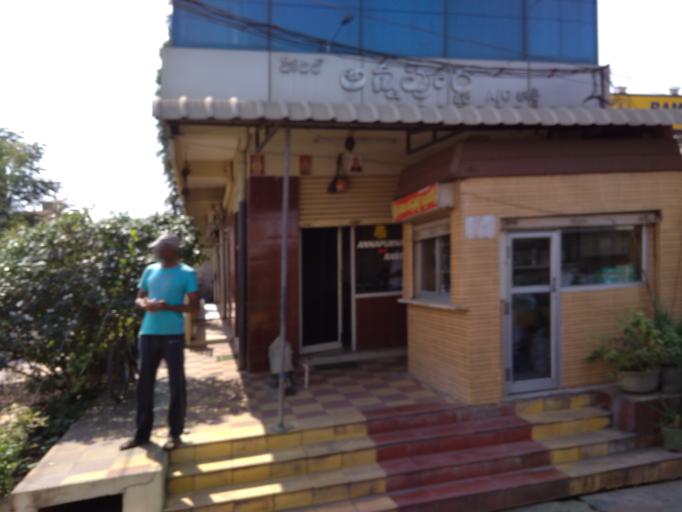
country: IN
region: Andhra Pradesh
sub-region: Krishna
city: Yanamalakuduru
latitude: 16.5178
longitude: 80.6979
